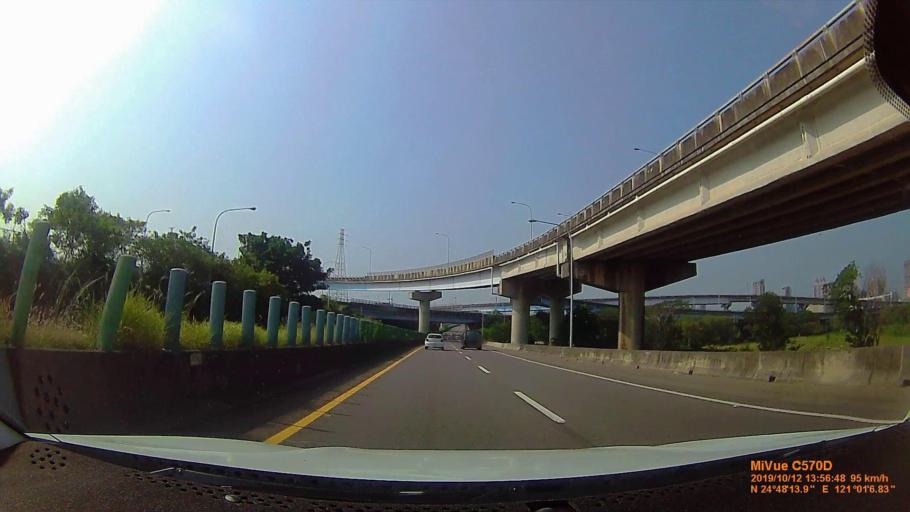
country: TW
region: Taiwan
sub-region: Hsinchu
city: Zhubei
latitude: 24.8040
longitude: 121.0182
